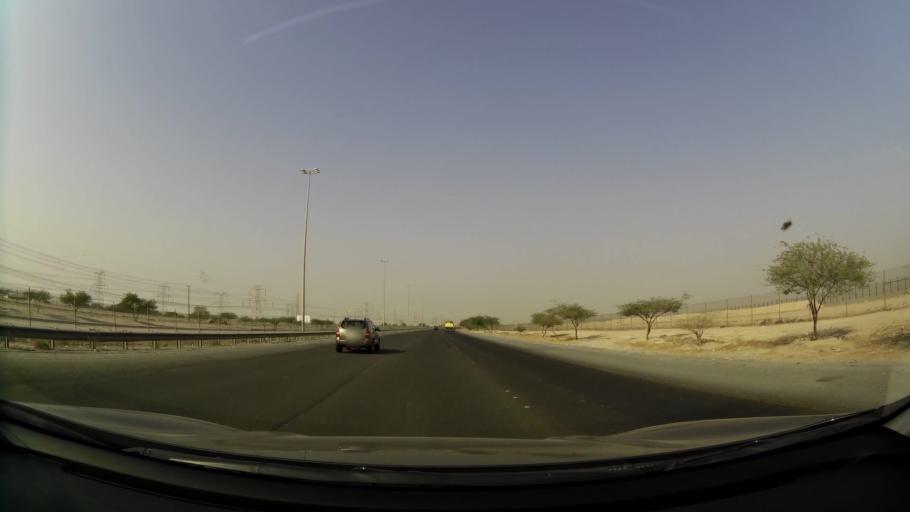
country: KW
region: Al Farwaniyah
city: Al Farwaniyah
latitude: 29.1819
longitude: 47.9206
